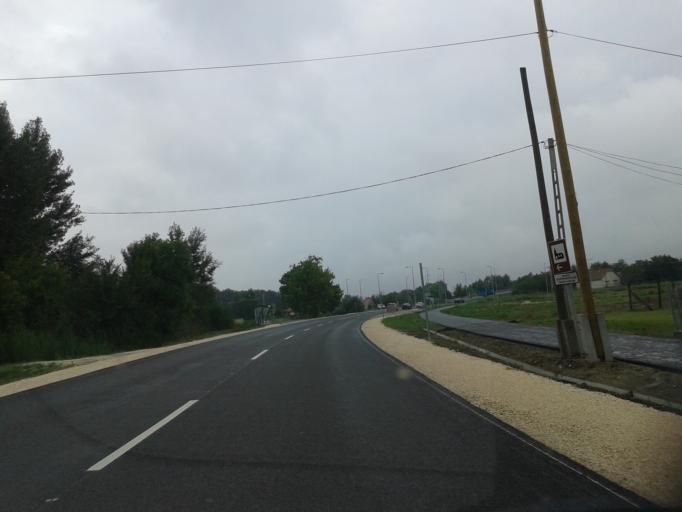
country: HU
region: Csongrad
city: Domaszek
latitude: 46.2465
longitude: 20.0290
